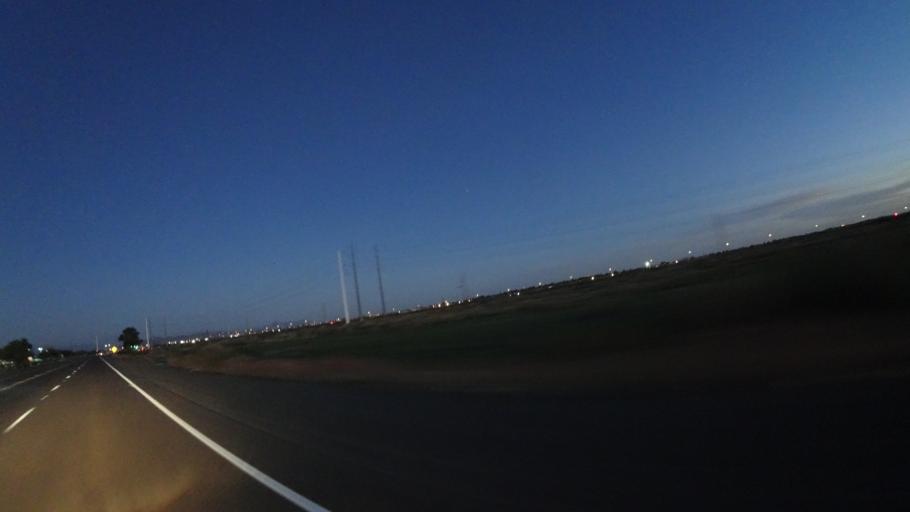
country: US
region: Arizona
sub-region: Maricopa County
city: Mesa
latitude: 33.4542
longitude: -111.8633
